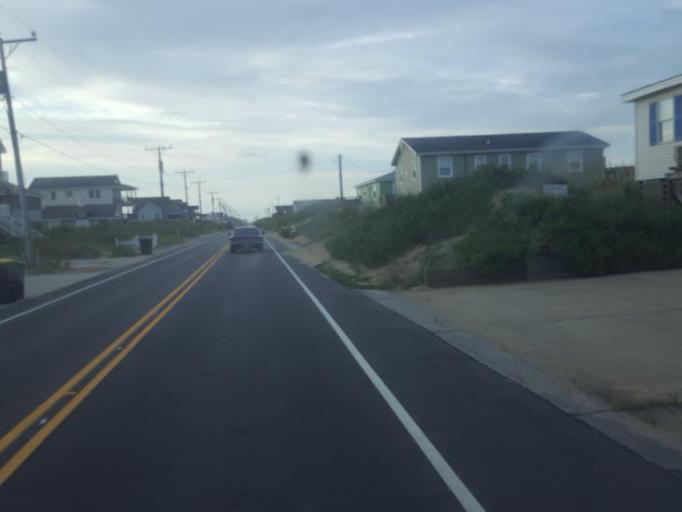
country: US
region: North Carolina
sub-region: Dare County
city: Kill Devil Hills
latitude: 36.0533
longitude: -75.6814
